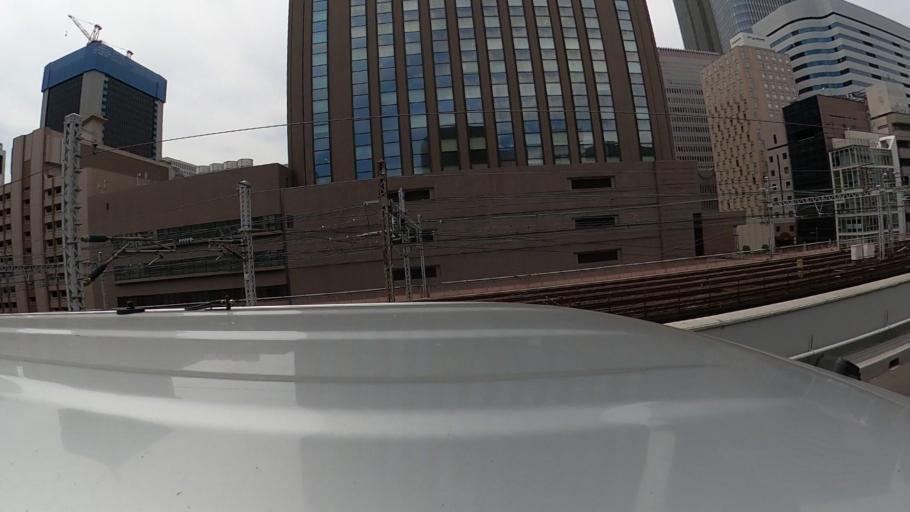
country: JP
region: Tokyo
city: Tokyo
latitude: 35.6714
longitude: 139.7601
